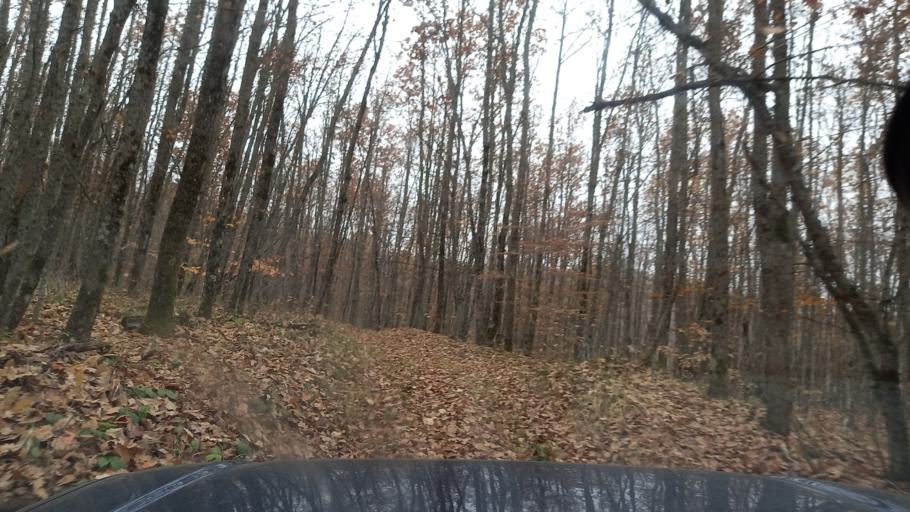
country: RU
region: Krasnodarskiy
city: Goryachiy Klyuch
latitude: 44.4978
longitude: 39.2770
